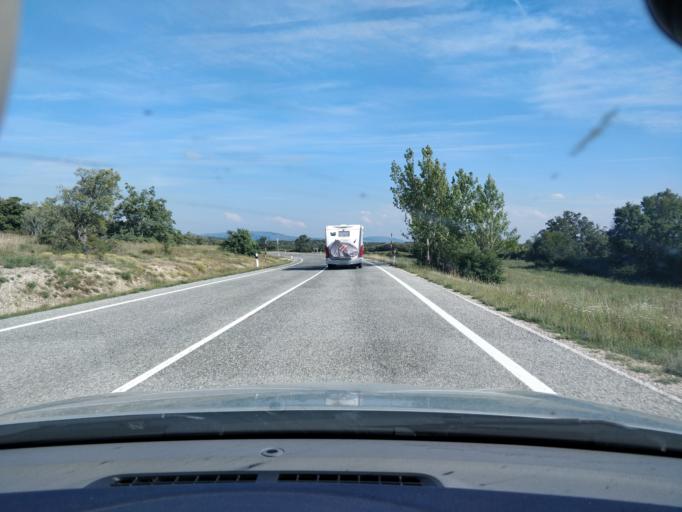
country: ES
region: Cantabria
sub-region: Provincia de Cantabria
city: San Martin de Elines
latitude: 42.9459
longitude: -3.7520
